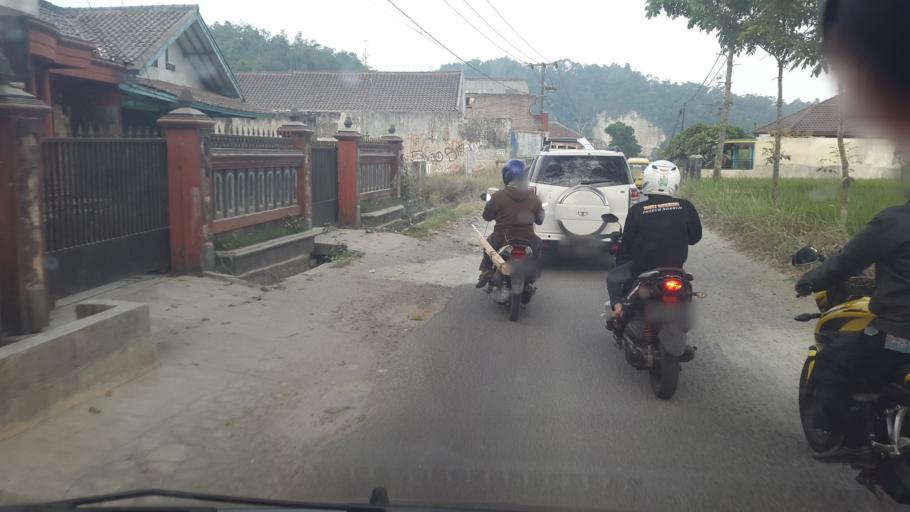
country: ID
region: West Java
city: Pasirreungit
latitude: -6.9429
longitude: 107.0027
